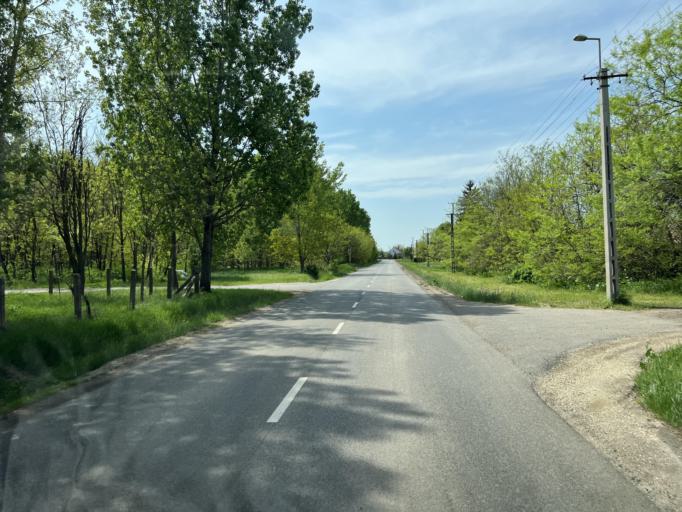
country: HU
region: Pest
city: Abony
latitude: 47.2074
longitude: 20.0106
